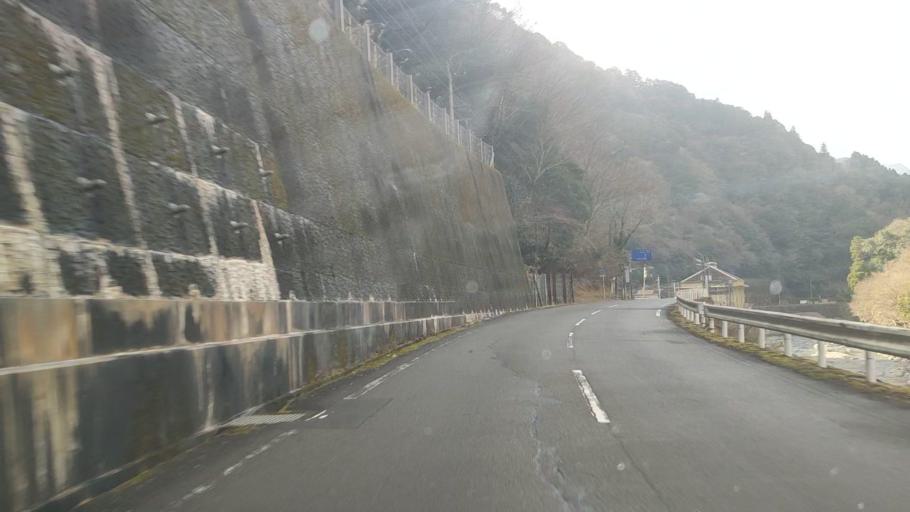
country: JP
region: Kumamoto
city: Hitoyoshi
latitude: 32.4209
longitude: 130.8551
